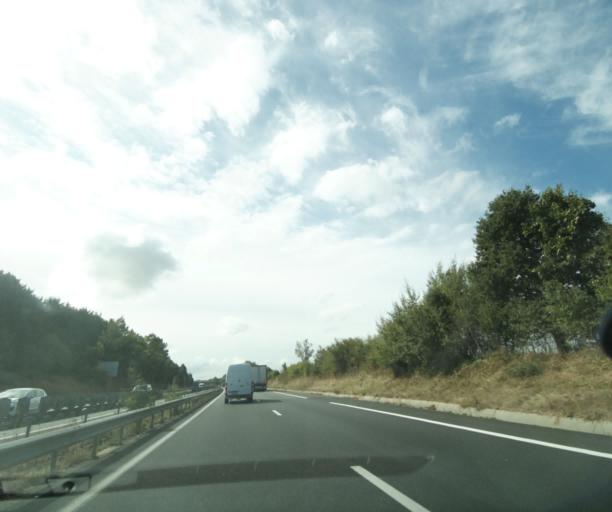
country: FR
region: Poitou-Charentes
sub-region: Departement de la Charente-Maritime
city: Pons
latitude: 45.5840
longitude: -0.5966
